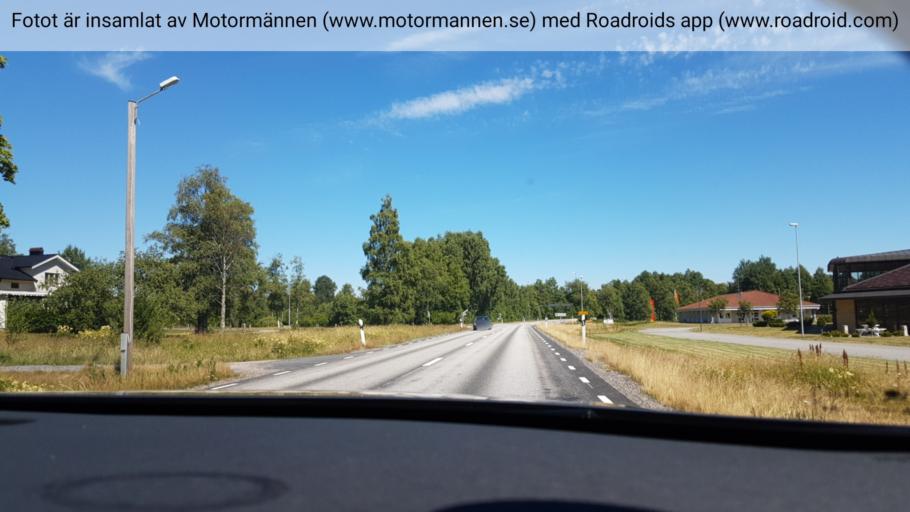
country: SE
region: Joenkoeping
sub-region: Gnosjo Kommun
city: Hillerstorp
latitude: 57.3216
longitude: 13.8722
